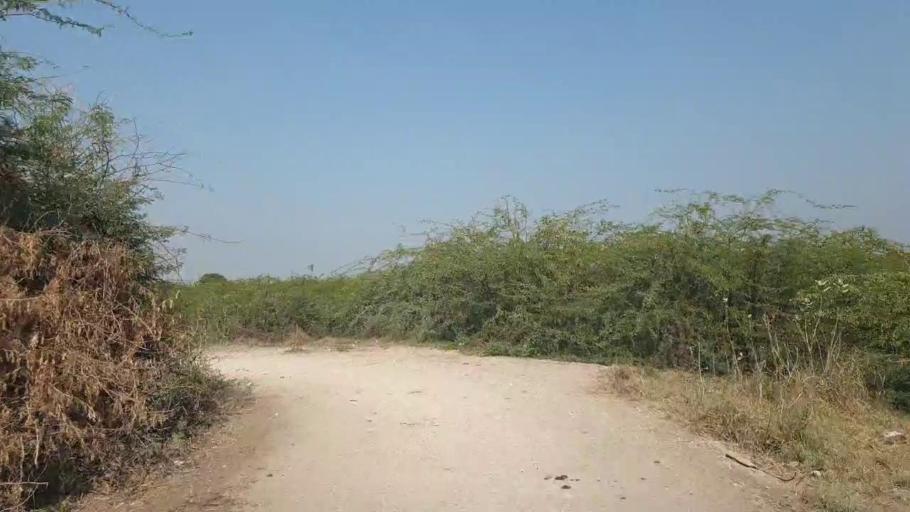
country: PK
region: Sindh
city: Chambar
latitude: 25.4115
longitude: 68.9074
